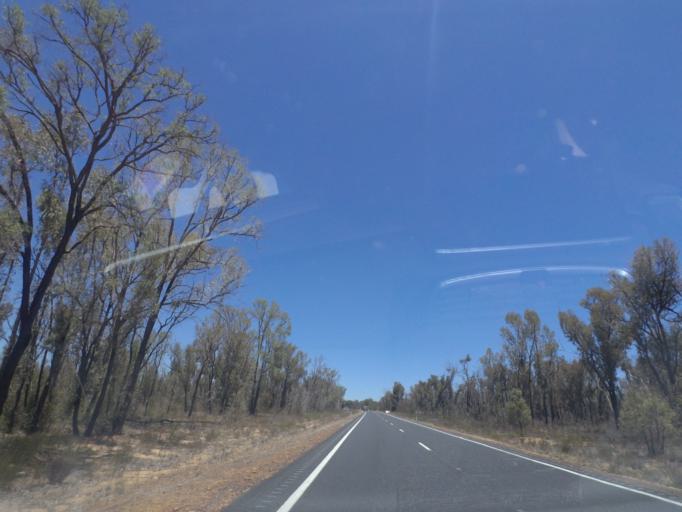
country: AU
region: New South Wales
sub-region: Warrumbungle Shire
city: Coonabarabran
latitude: -30.9395
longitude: 149.4246
